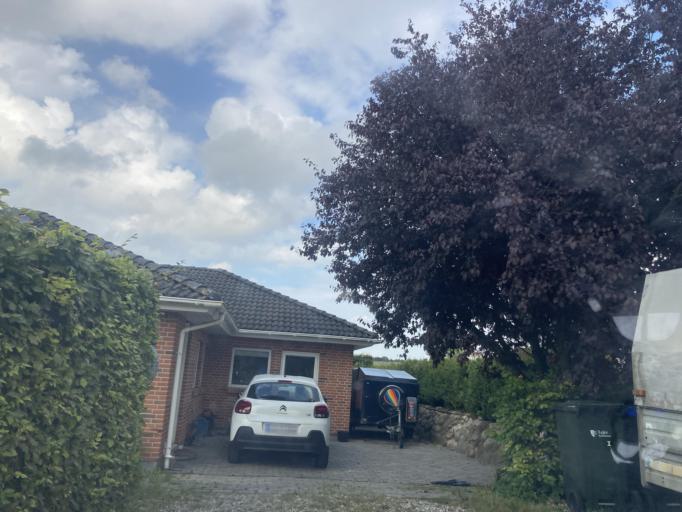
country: DK
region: Zealand
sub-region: Roskilde Kommune
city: Svogerslev
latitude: 55.5981
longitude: 12.0121
